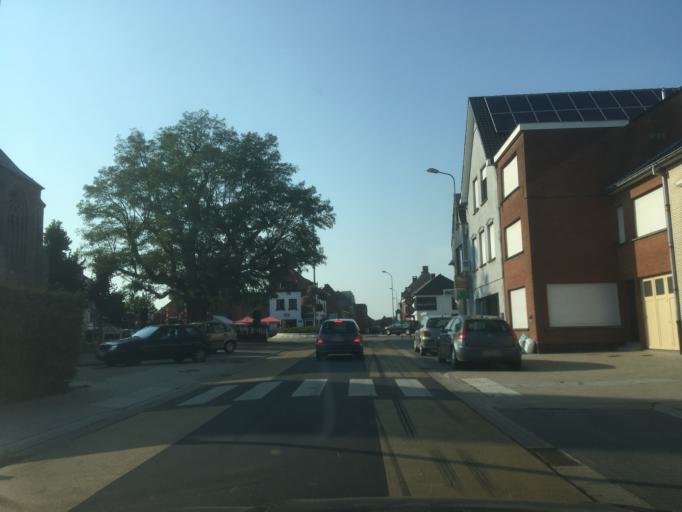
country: BE
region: Flanders
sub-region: Provincie West-Vlaanderen
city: Oostrozebeke
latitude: 50.8929
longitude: 3.3372
